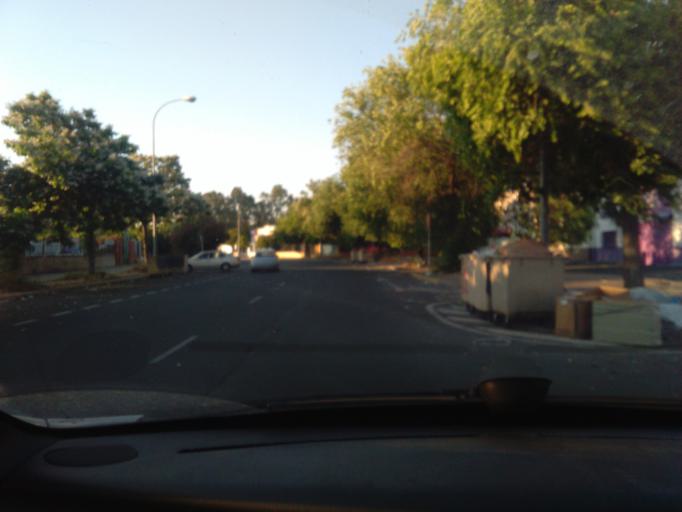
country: ES
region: Andalusia
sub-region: Provincia de Sevilla
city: Sevilla
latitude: 37.3943
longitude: -5.9415
